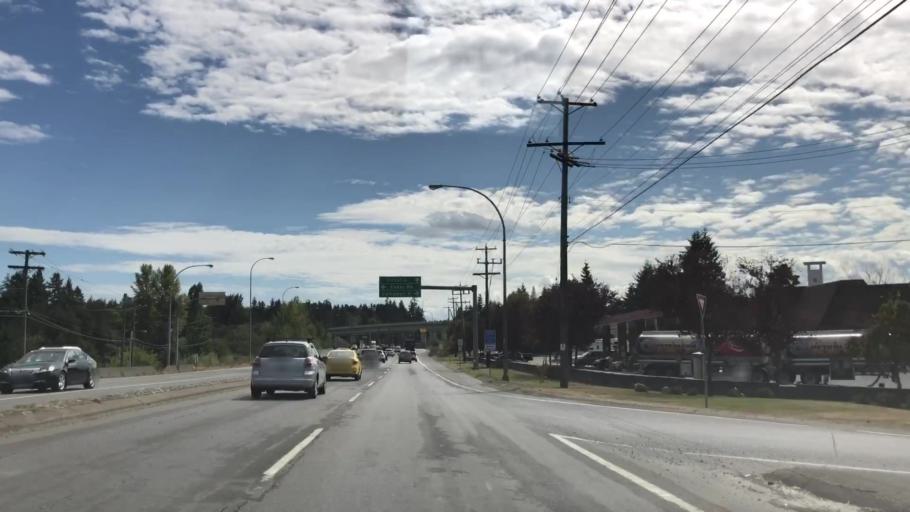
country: CA
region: British Columbia
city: Nanaimo
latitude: 49.1278
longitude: -123.9196
